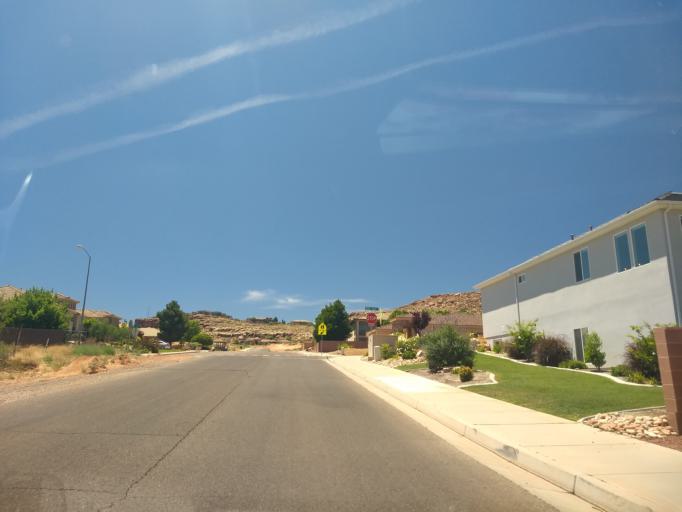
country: US
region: Utah
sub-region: Washington County
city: Washington
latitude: 37.0742
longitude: -113.5309
